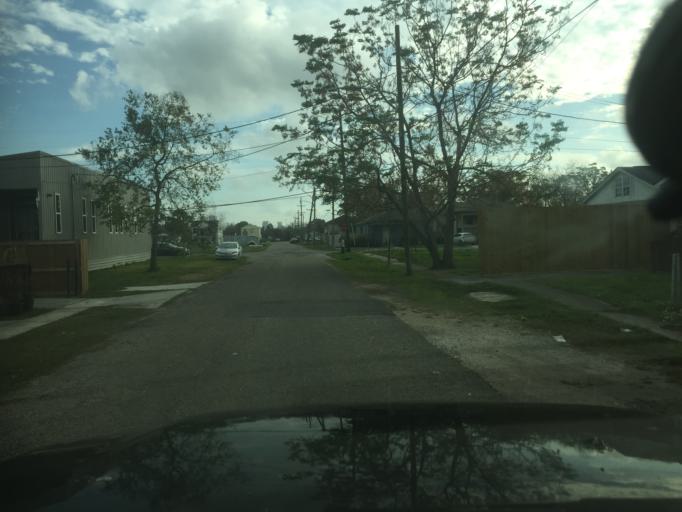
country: US
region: Louisiana
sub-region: Orleans Parish
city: New Orleans
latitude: 29.9962
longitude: -90.0807
